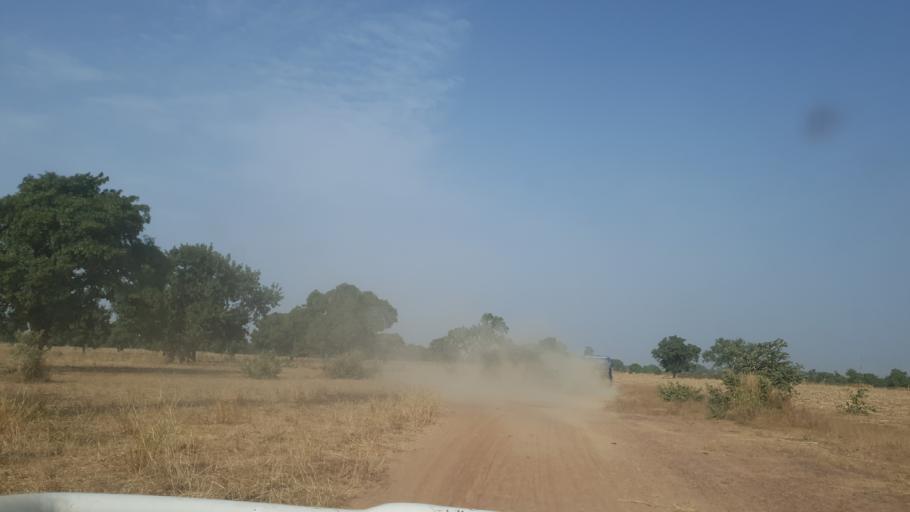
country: ML
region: Segou
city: Baroueli
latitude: 13.3504
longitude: -6.9418
